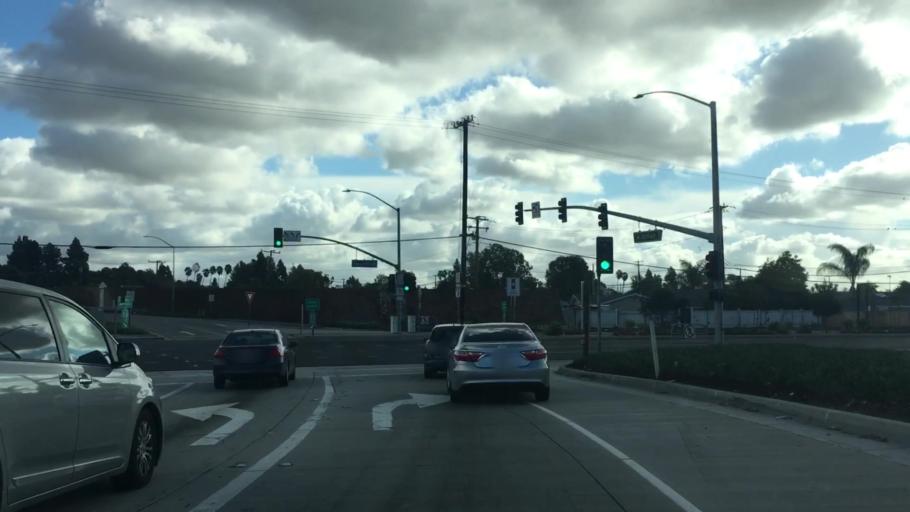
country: US
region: California
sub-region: Orange County
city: Midway City
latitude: 33.7652
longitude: -117.9729
